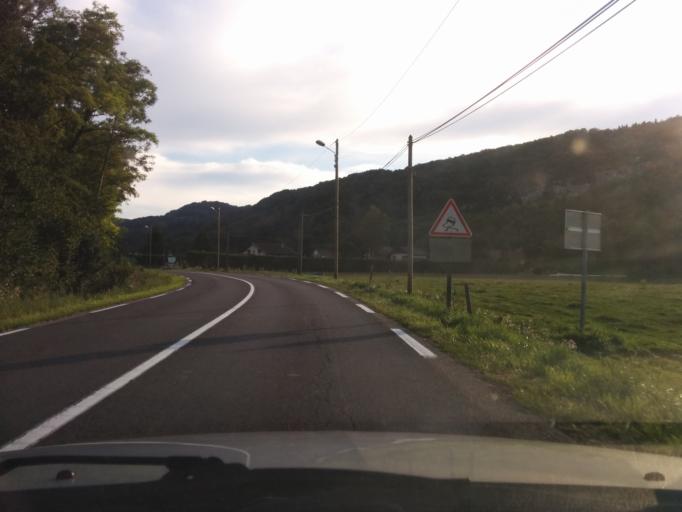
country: FR
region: Rhone-Alpes
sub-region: Departement de l'Isere
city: Saint-Aupre
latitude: 45.3612
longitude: 5.6775
